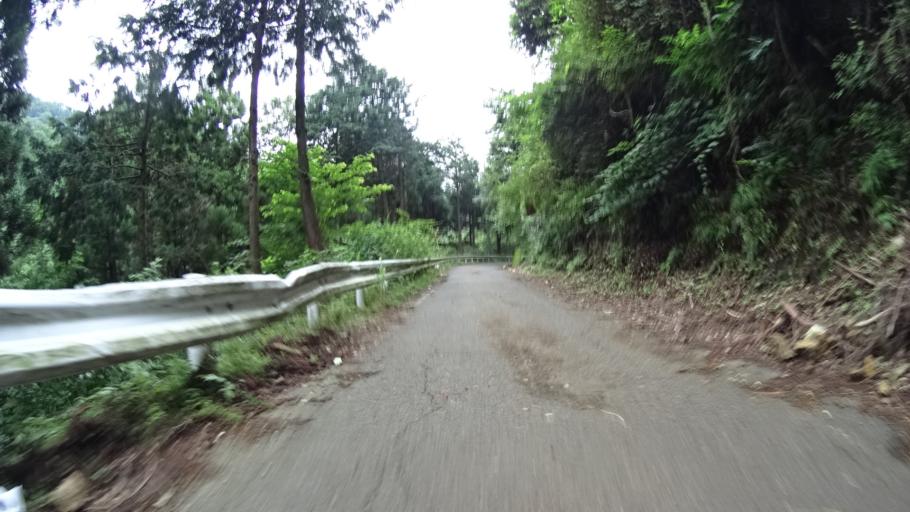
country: JP
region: Kanagawa
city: Atsugi
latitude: 35.5022
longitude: 139.2722
